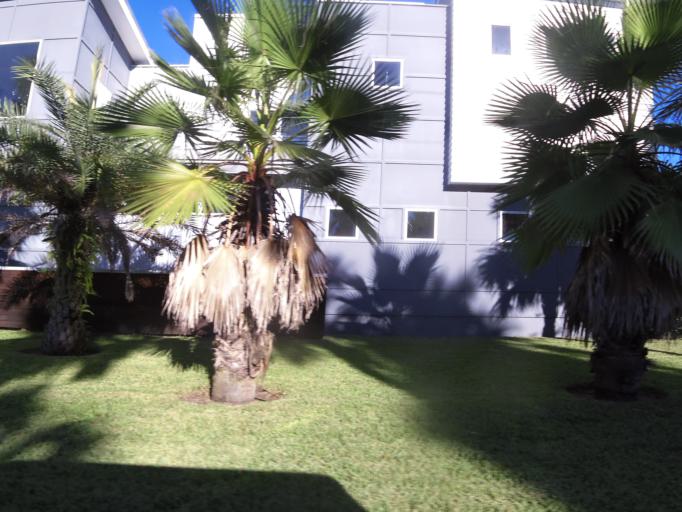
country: US
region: Florida
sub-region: Duval County
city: Atlantic Beach
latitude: 30.3333
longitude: -81.3982
